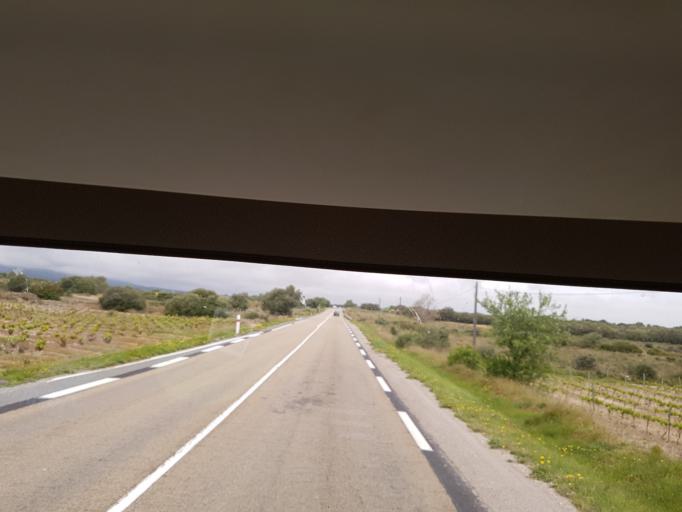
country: FR
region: Languedoc-Roussillon
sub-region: Departement de l'Aude
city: Leucate
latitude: 42.9153
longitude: 2.9977
